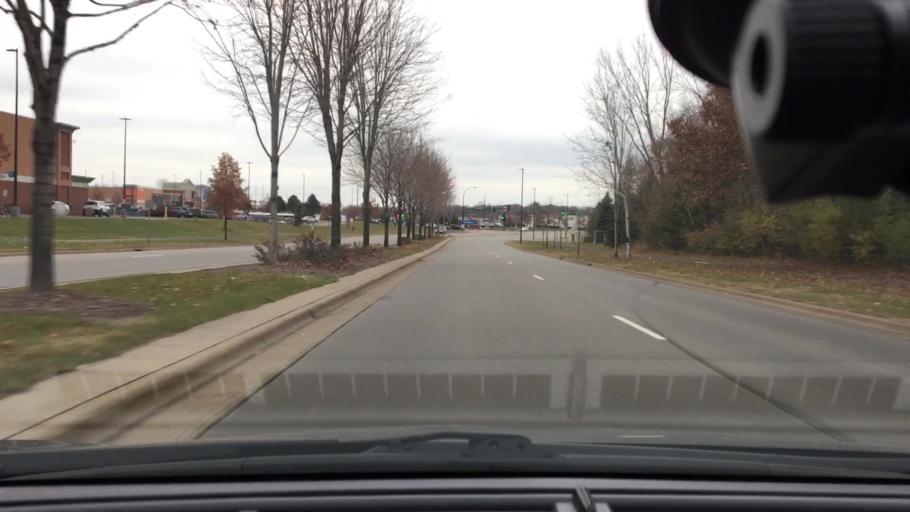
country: US
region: Minnesota
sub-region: Hennepin County
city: Corcoran
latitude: 45.1226
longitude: -93.4923
